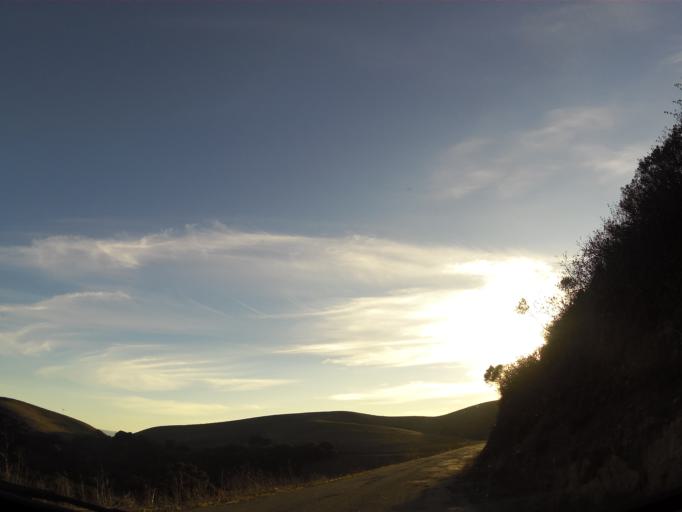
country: US
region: California
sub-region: San Benito County
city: San Juan Bautista
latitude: 36.8185
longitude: -121.5741
